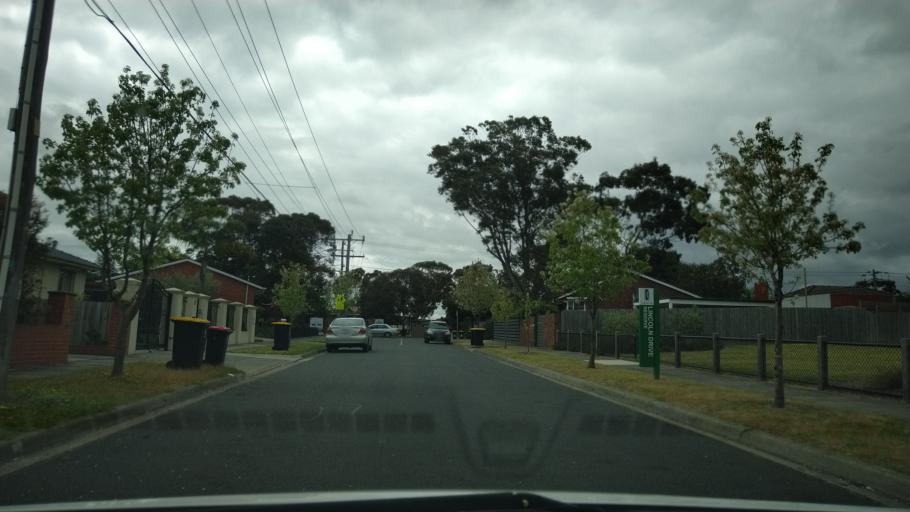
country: AU
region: Victoria
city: Heatherton
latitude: -37.9638
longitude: 145.0789
